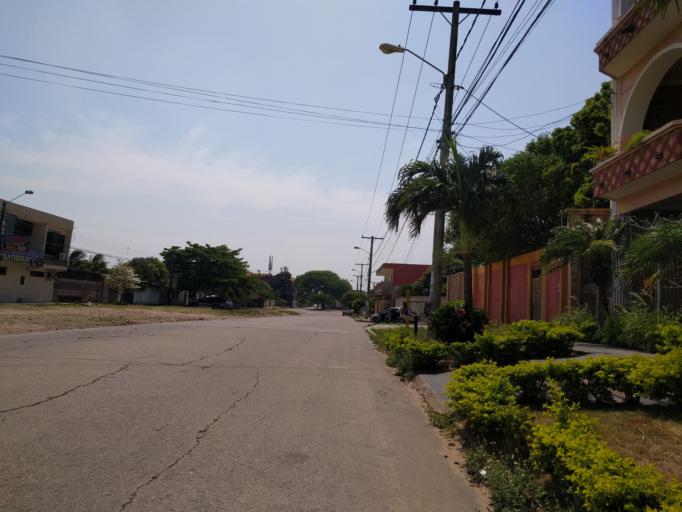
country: BO
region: Santa Cruz
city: Santa Cruz de la Sierra
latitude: -17.7914
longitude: -63.1518
